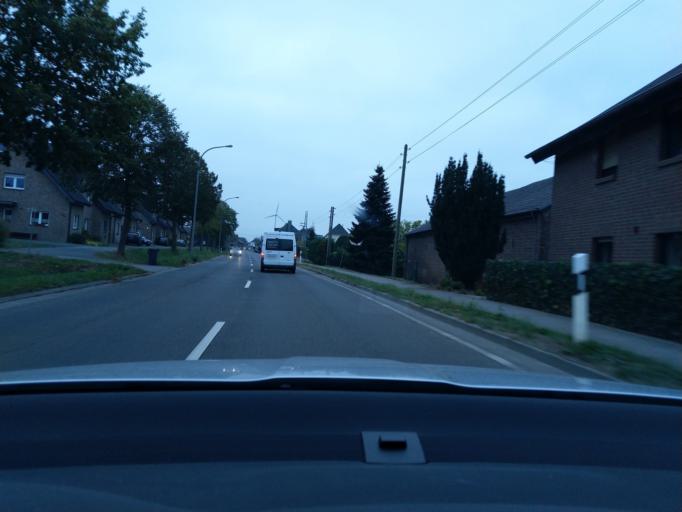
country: DE
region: North Rhine-Westphalia
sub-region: Regierungsbezirk Dusseldorf
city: Schwalmtal
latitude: 51.2338
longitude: 6.3093
